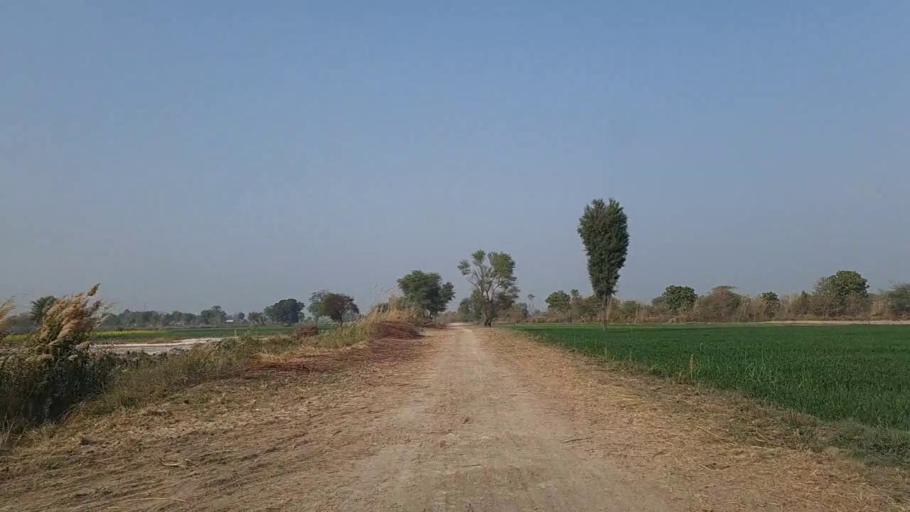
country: PK
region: Sindh
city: Nawabshah
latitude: 26.3524
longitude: 68.4741
